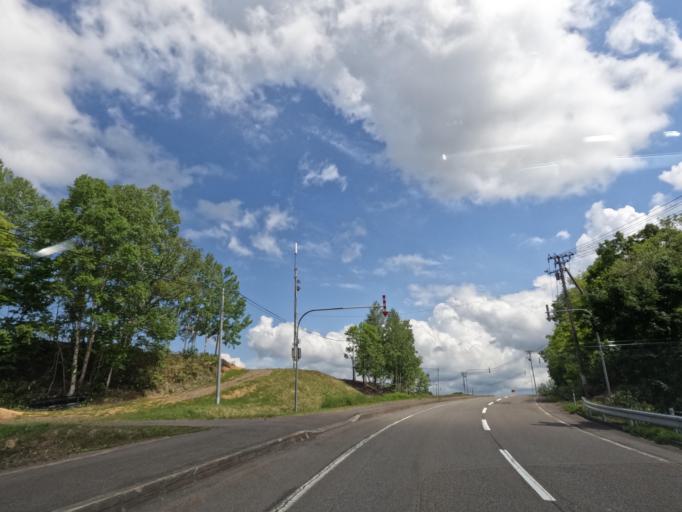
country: JP
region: Hokkaido
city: Takikawa
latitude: 43.5818
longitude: 141.8191
